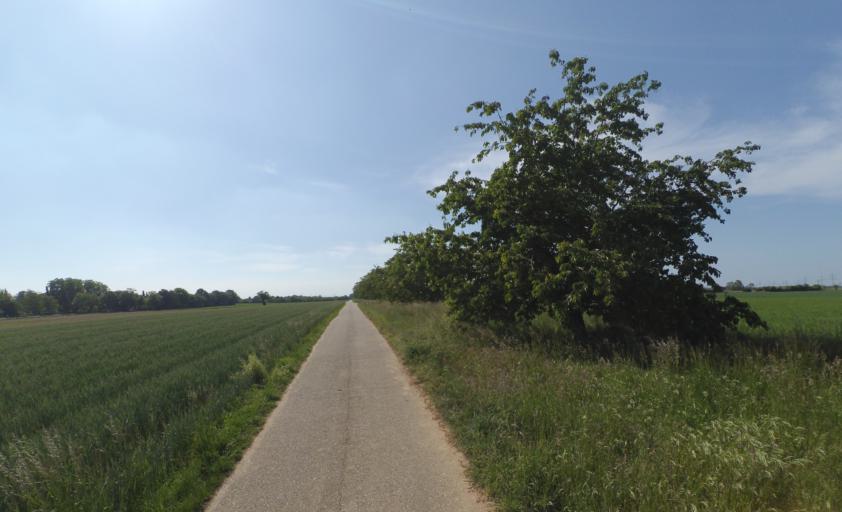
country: DE
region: Baden-Wuerttemberg
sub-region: Karlsruhe Region
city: Plankstadt
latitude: 49.4005
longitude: 8.6013
